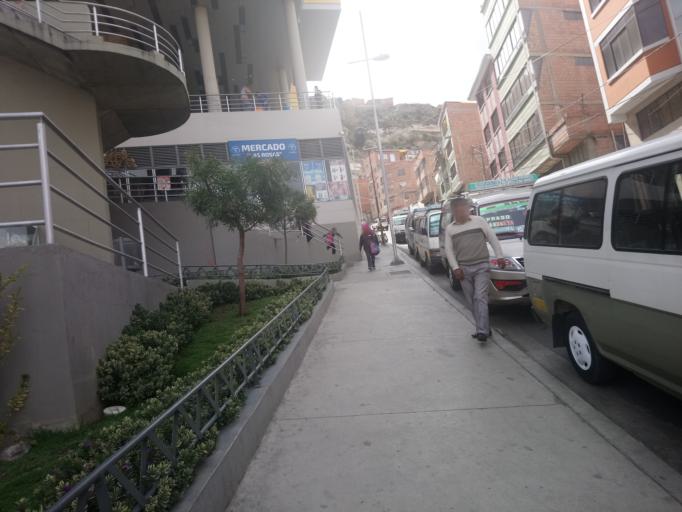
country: BO
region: La Paz
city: La Paz
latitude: -16.5154
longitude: -68.1439
